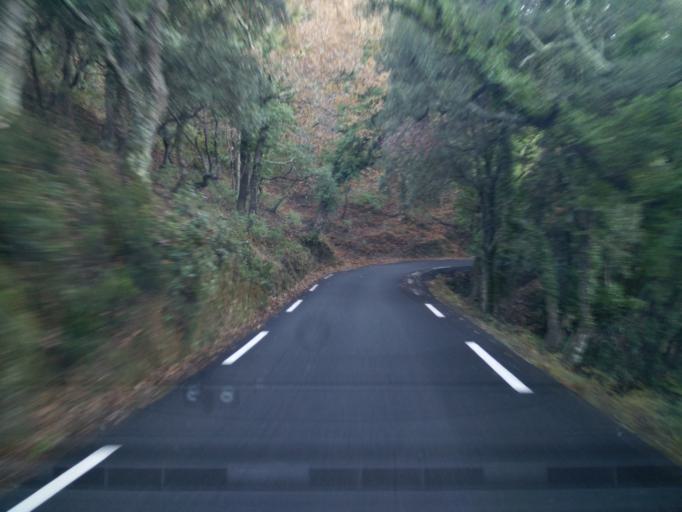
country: FR
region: Provence-Alpes-Cote d'Azur
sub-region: Departement du Var
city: Collobrieres
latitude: 43.2397
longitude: 6.3384
